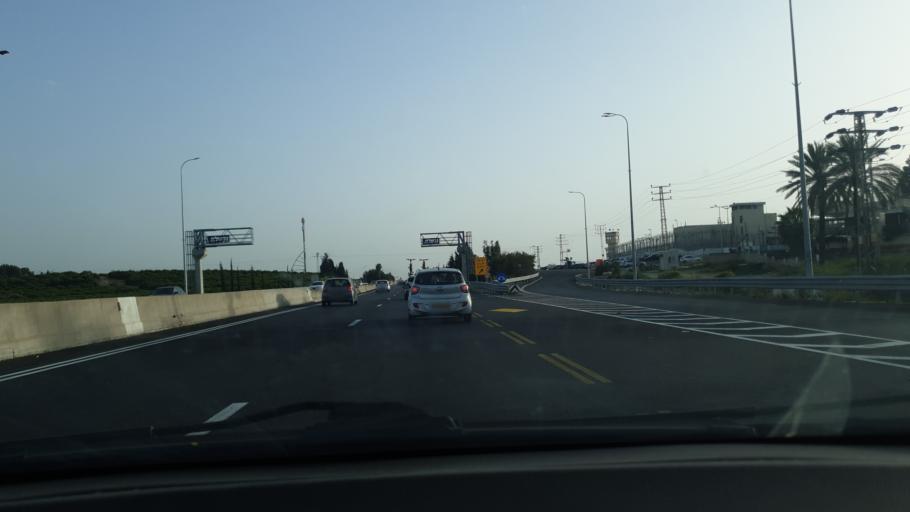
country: IL
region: Central District
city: Even Yehuda
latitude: 32.2410
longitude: 34.8870
